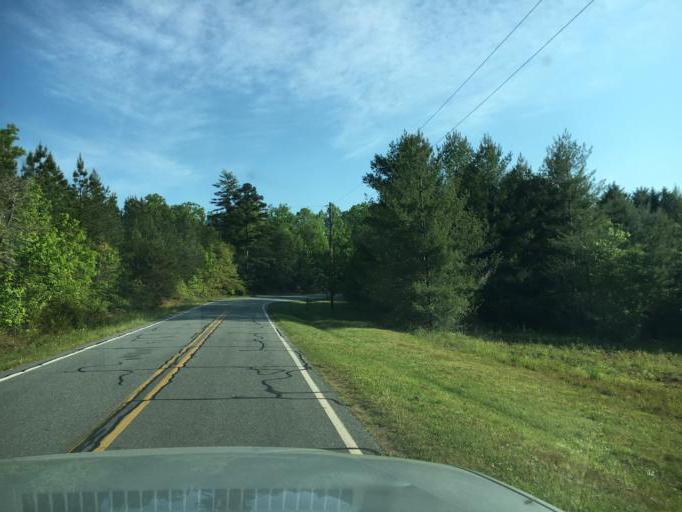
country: US
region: North Carolina
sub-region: Rutherford County
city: Rutherfordton
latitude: 35.3342
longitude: -81.9890
